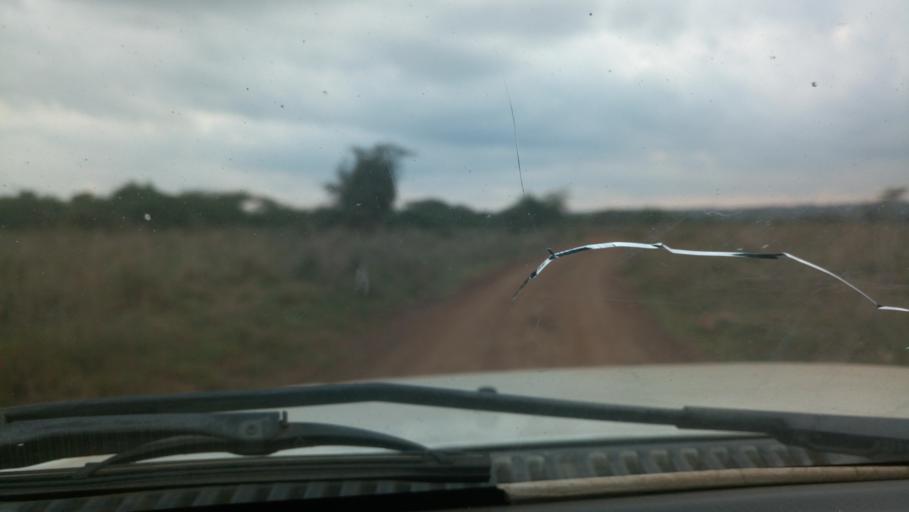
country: KE
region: Nairobi Area
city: Nairobi
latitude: -1.3452
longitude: 36.8148
